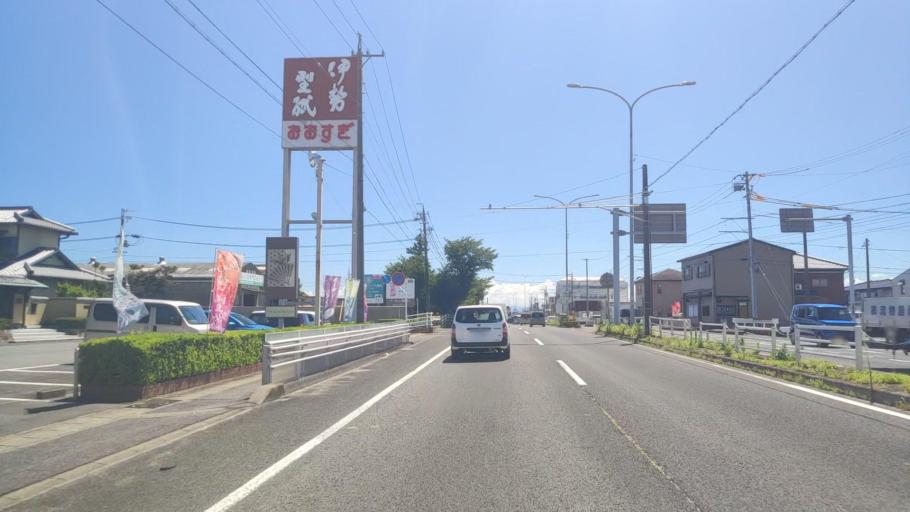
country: JP
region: Mie
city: Kawage
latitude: 34.8330
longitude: 136.5845
